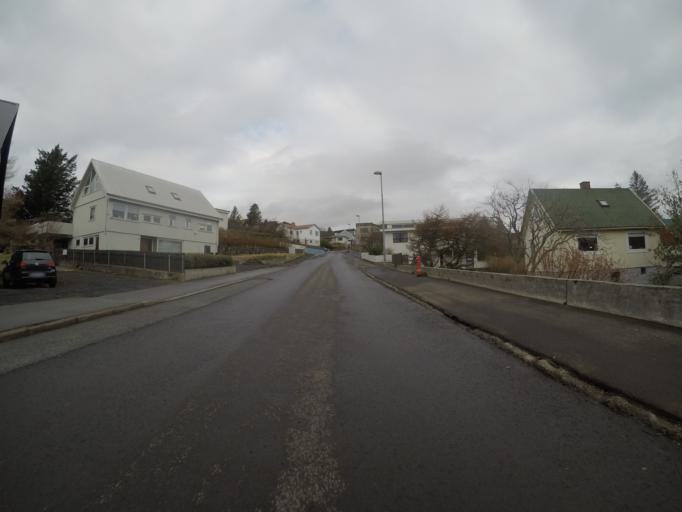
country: FO
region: Streymoy
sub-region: Torshavn
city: Torshavn
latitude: 62.0144
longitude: -6.7805
